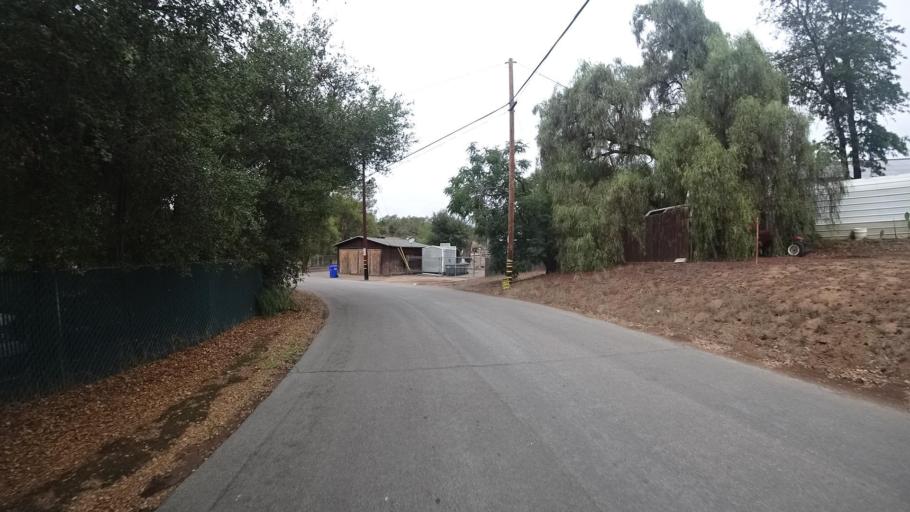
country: US
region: California
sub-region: San Diego County
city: Ramona
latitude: 33.0709
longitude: -116.8849
